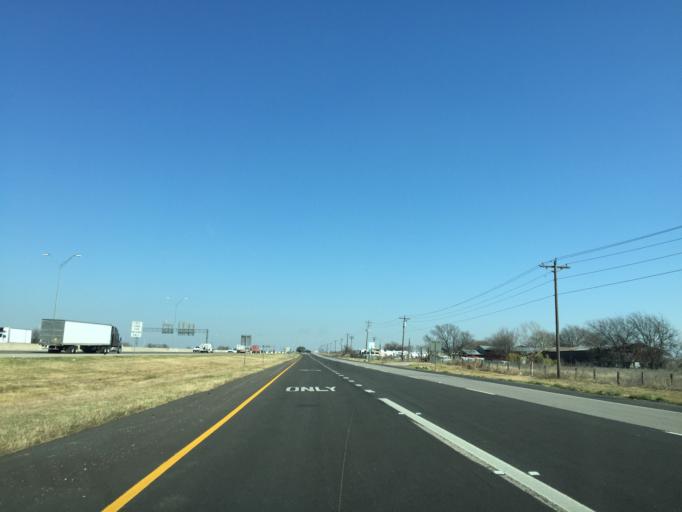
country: US
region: Texas
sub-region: Williamson County
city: Serenada
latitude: 30.7105
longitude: -97.6483
